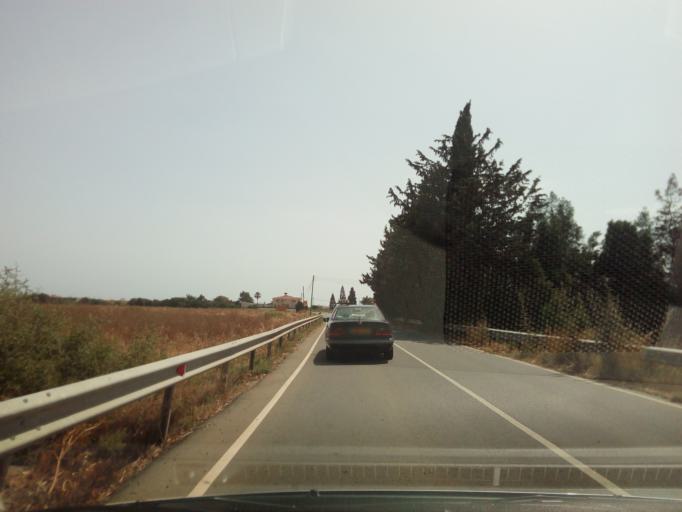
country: CY
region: Larnaka
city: Perivolia
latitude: 34.8380
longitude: 33.5885
